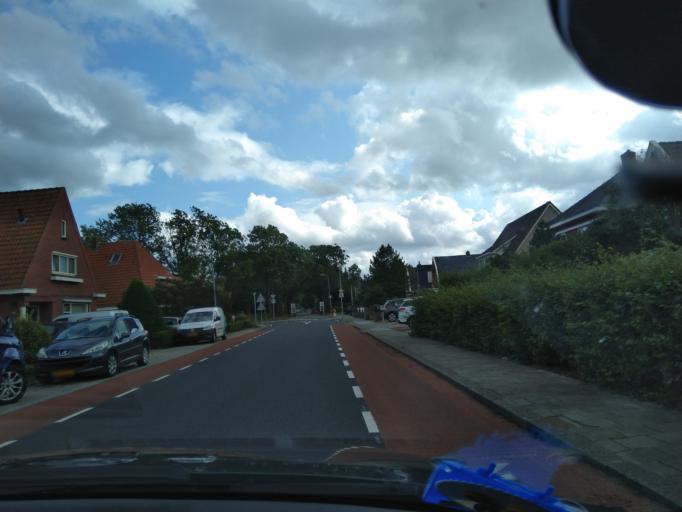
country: NL
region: Groningen
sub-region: Gemeente Zuidhorn
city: Aduard
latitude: 53.2271
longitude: 6.5001
